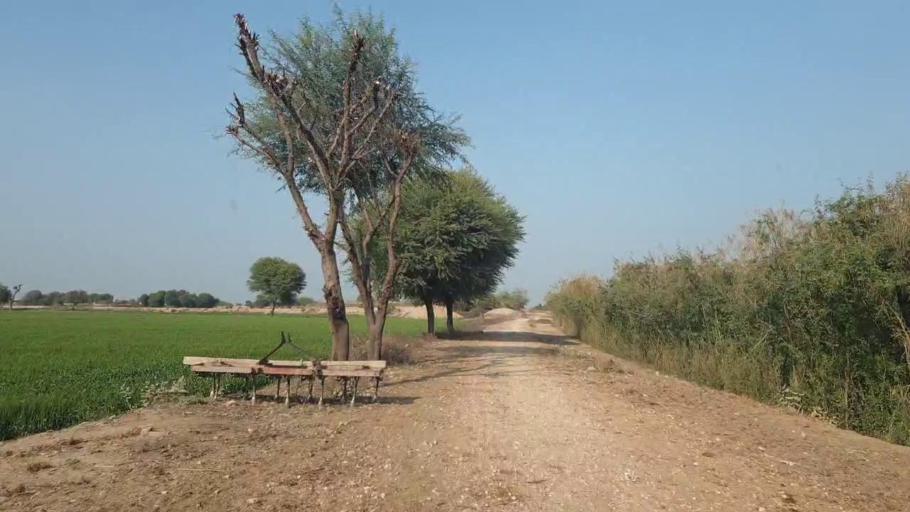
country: PK
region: Sindh
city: Hala
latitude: 25.8345
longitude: 68.4038
